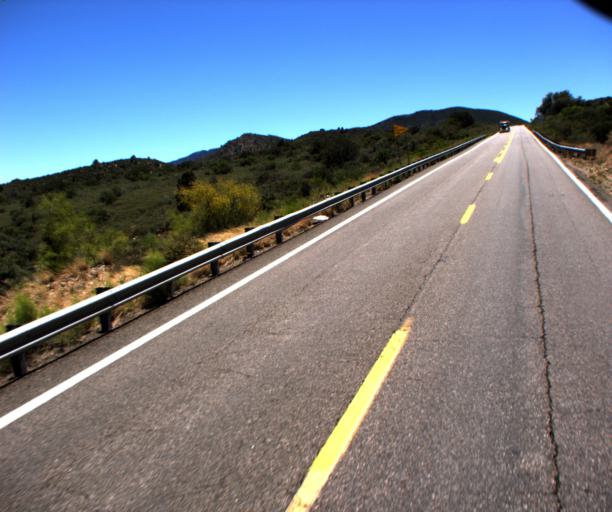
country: US
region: Arizona
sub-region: Gila County
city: Globe
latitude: 33.2805
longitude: -110.7547
